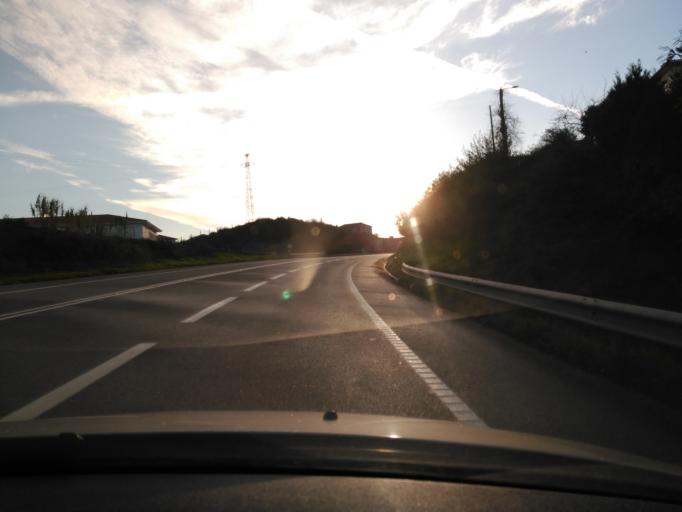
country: PT
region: Braga
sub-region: Fafe
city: Fafe
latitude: 41.4635
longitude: -8.1603
